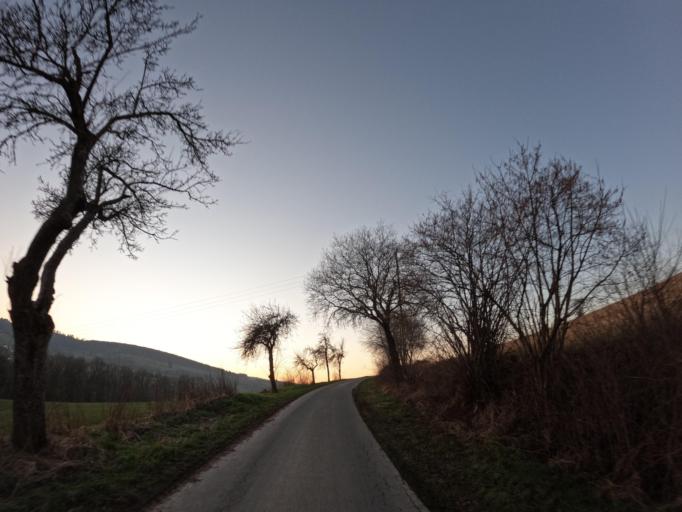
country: DE
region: Lower Saxony
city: Bodenfelde
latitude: 51.6807
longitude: 9.5872
